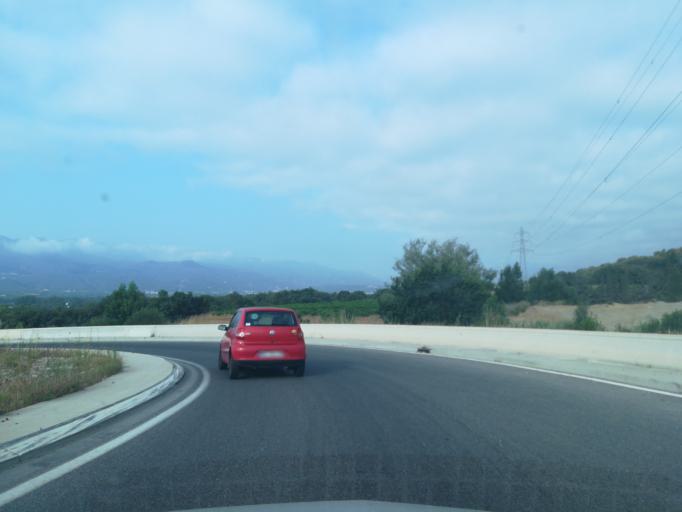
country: FR
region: Languedoc-Roussillon
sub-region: Departement des Pyrenees-Orientales
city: Sant Joan de Pladecorts
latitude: 42.5261
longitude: 2.8064
